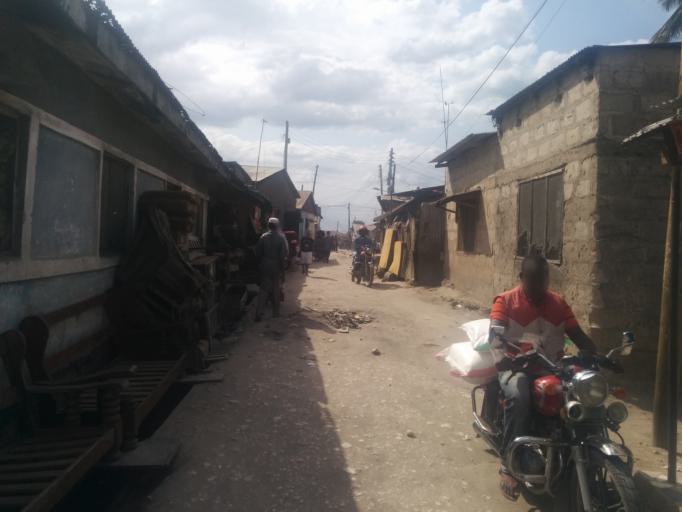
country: TZ
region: Dar es Salaam
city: Magomeni
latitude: -6.7974
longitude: 39.2356
